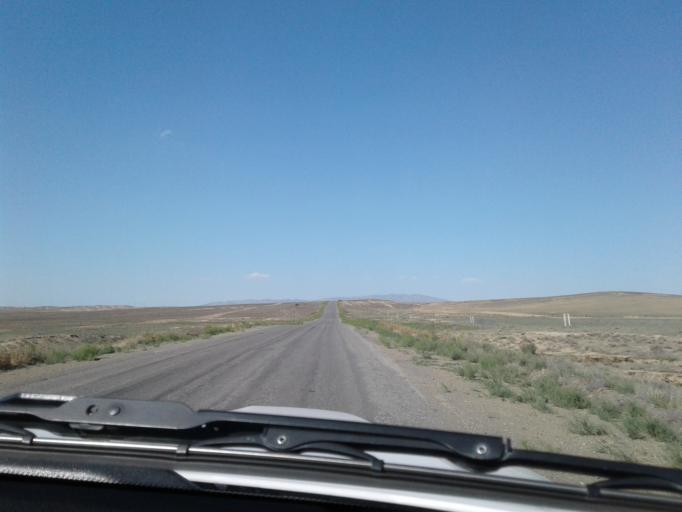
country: TM
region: Balkan
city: Magtymguly
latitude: 38.6315
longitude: 56.2424
